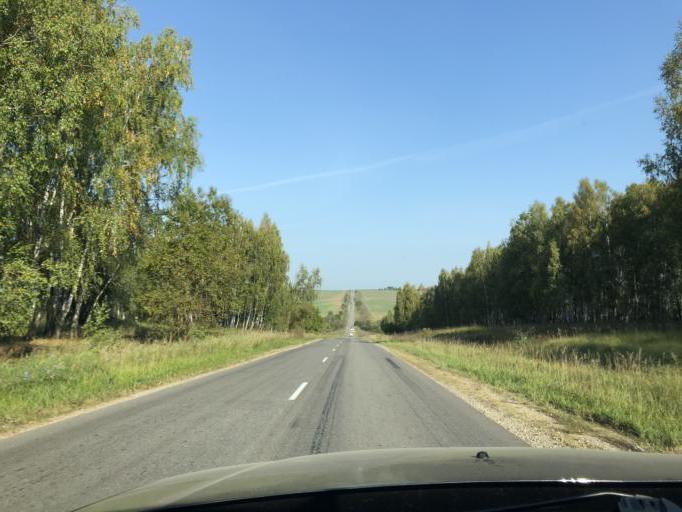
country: RU
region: Tula
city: Novogurovskiy
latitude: 54.3893
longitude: 37.3228
